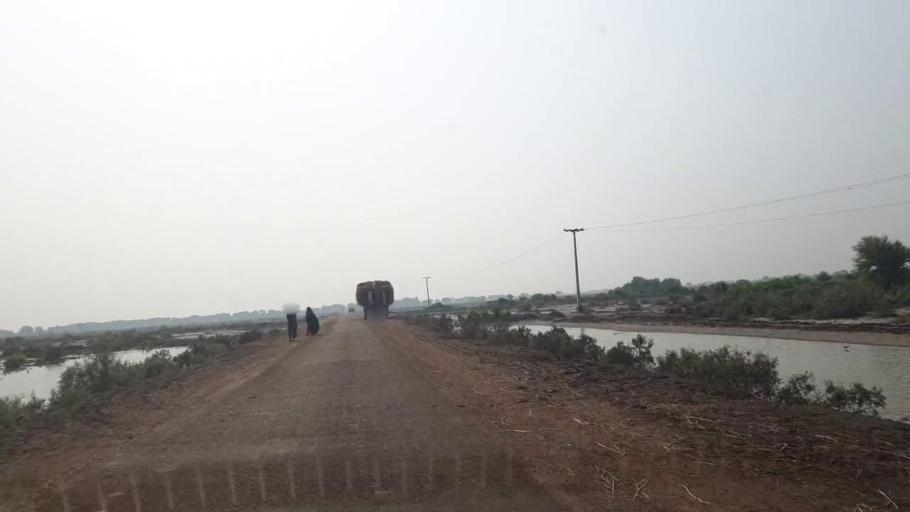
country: PK
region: Sindh
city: Matli
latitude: 25.1353
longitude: 68.6906
